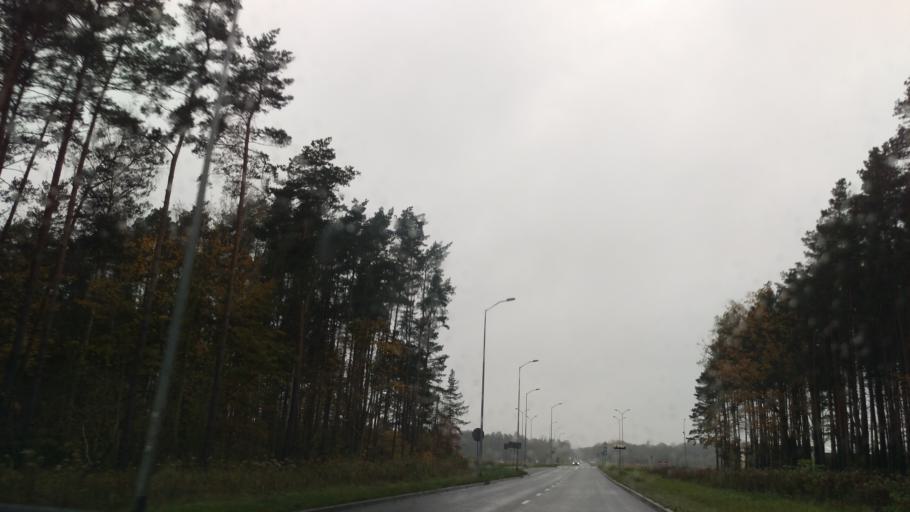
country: PL
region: West Pomeranian Voivodeship
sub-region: Powiat gryfinski
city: Stare Czarnowo
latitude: 53.3992
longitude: 14.7094
